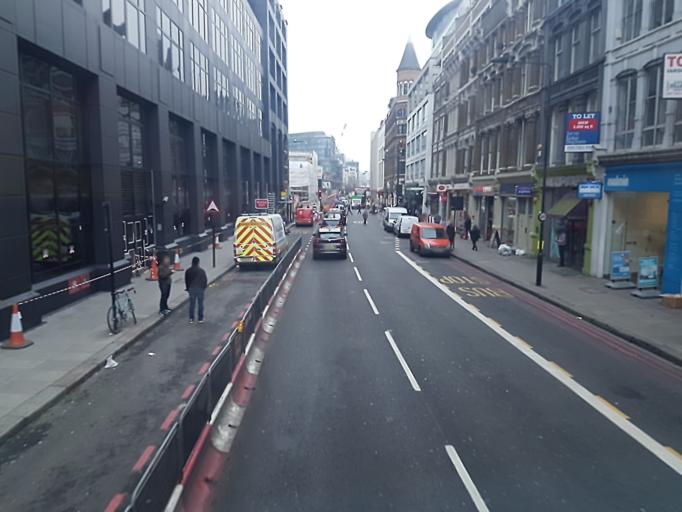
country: GB
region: England
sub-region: Greater London
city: Clerkenwell
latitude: 51.5206
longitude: -0.1060
